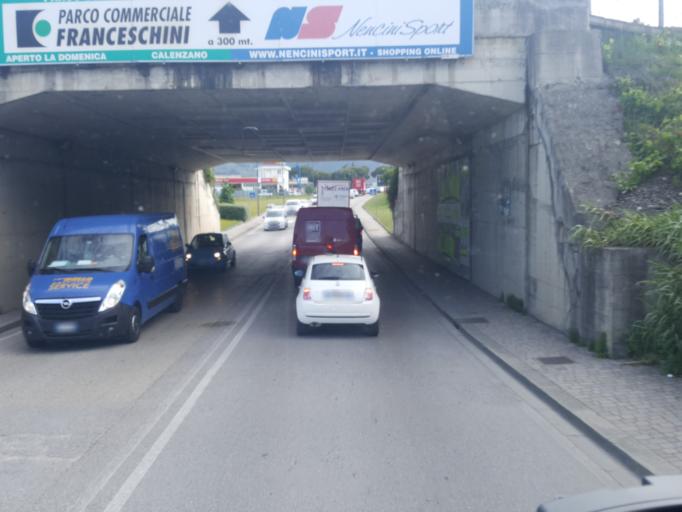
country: IT
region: Tuscany
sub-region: Province of Florence
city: Calenzano
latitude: 43.8487
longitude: 11.1624
